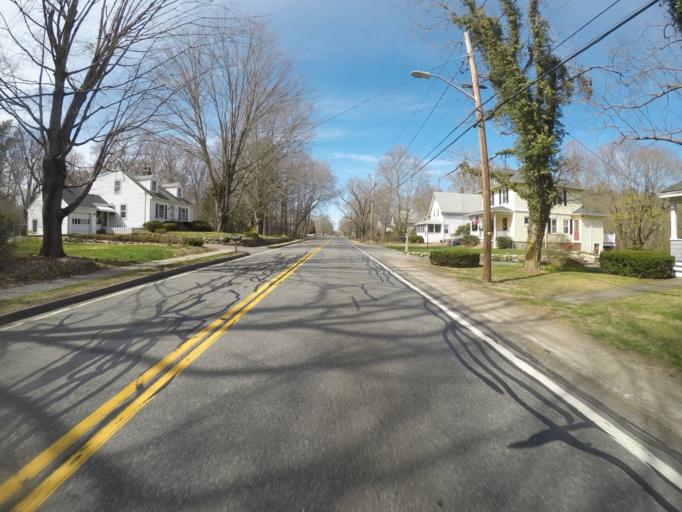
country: US
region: Massachusetts
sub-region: Plymouth County
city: West Bridgewater
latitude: 42.0316
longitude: -71.0667
